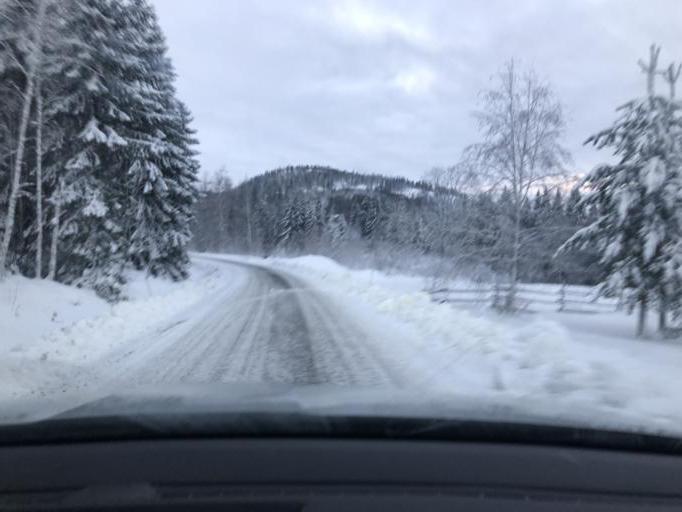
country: SE
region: Vaesternorrland
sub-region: Kramfors Kommun
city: Nordingra
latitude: 62.9086
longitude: 18.2400
